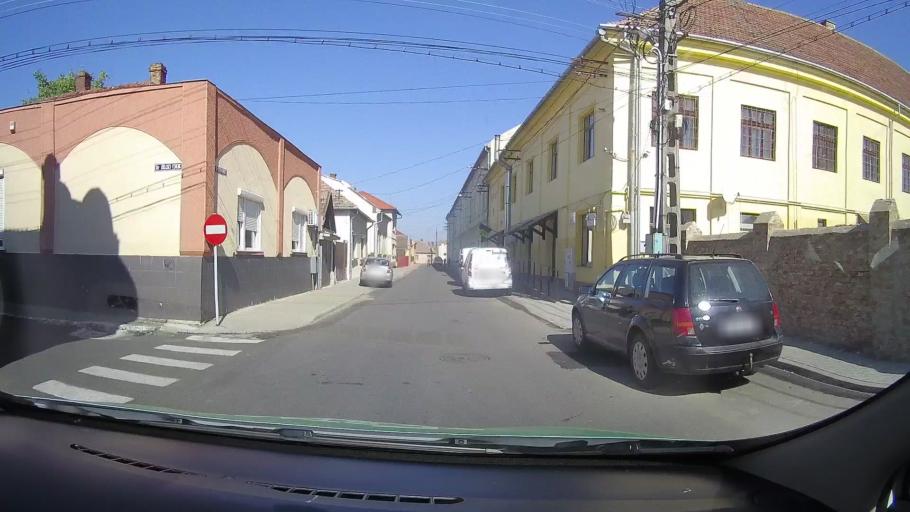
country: RO
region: Satu Mare
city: Carei
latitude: 47.6875
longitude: 22.4666
